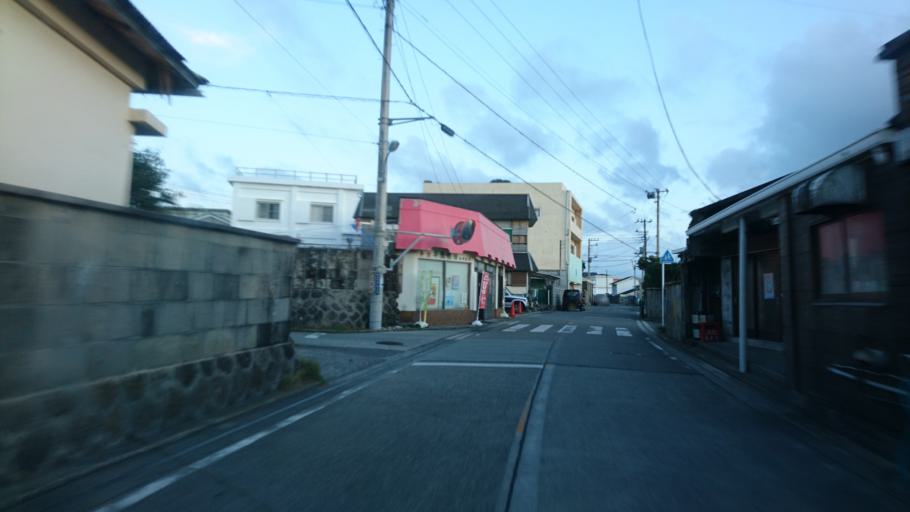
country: JP
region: Shizuoka
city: Shimoda
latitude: 34.3741
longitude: 139.2558
